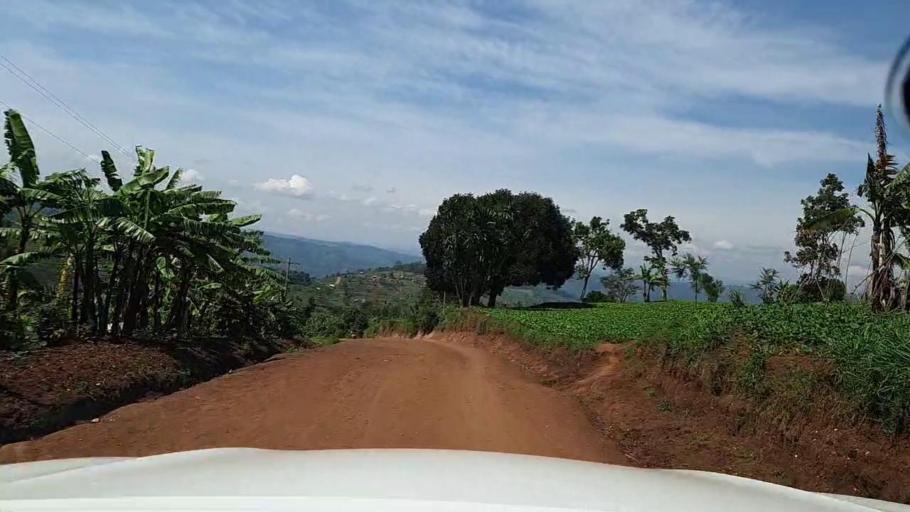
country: RW
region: Southern Province
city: Butare
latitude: -2.7216
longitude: 29.8361
